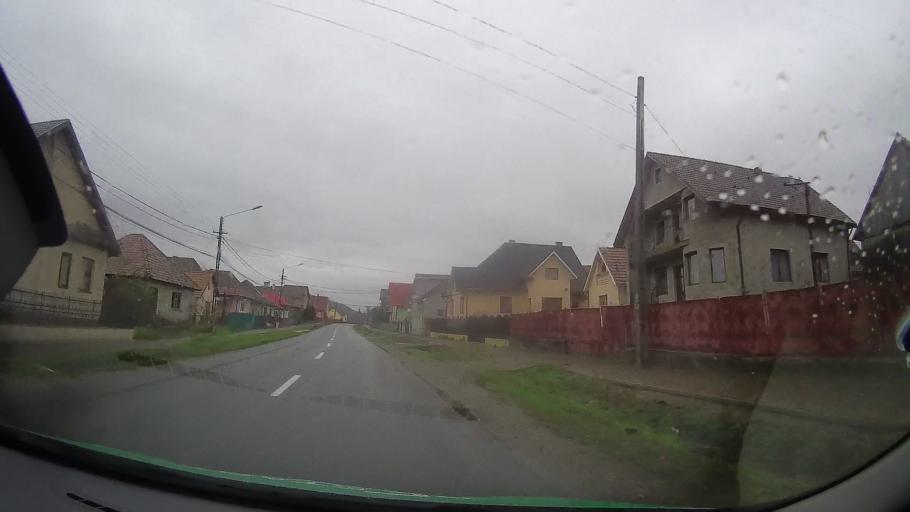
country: RO
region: Bistrita-Nasaud
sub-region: Municipiul Bistrita
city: Viisoara
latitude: 47.0743
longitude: 24.4356
